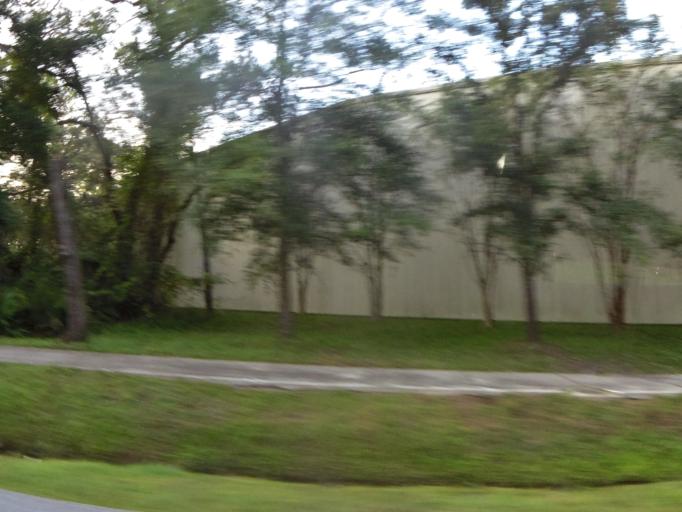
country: US
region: Florida
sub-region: Saint Johns County
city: Fruit Cove
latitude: 30.1796
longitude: -81.6307
